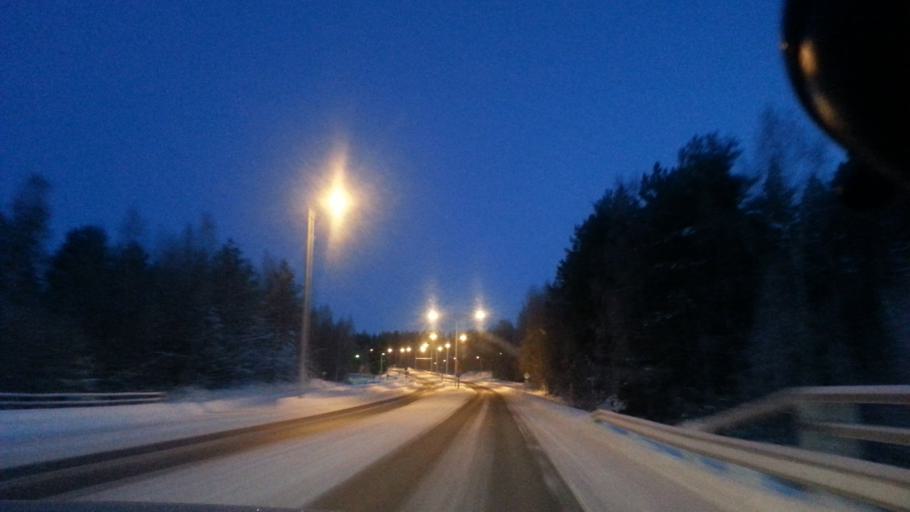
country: FI
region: Lapland
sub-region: Rovaniemi
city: Rovaniemi
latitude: 66.4886
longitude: 25.7541
